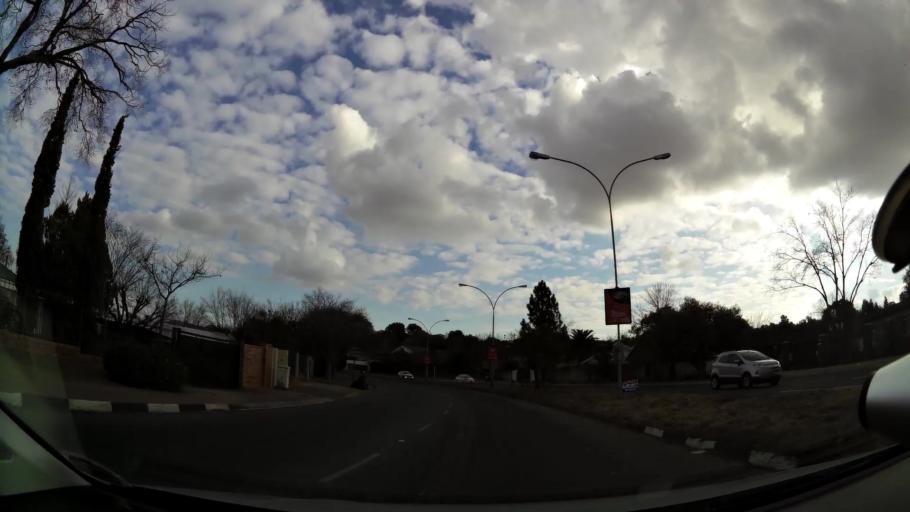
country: ZA
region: Orange Free State
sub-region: Mangaung Metropolitan Municipality
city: Bloemfontein
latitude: -29.0812
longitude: 26.2073
